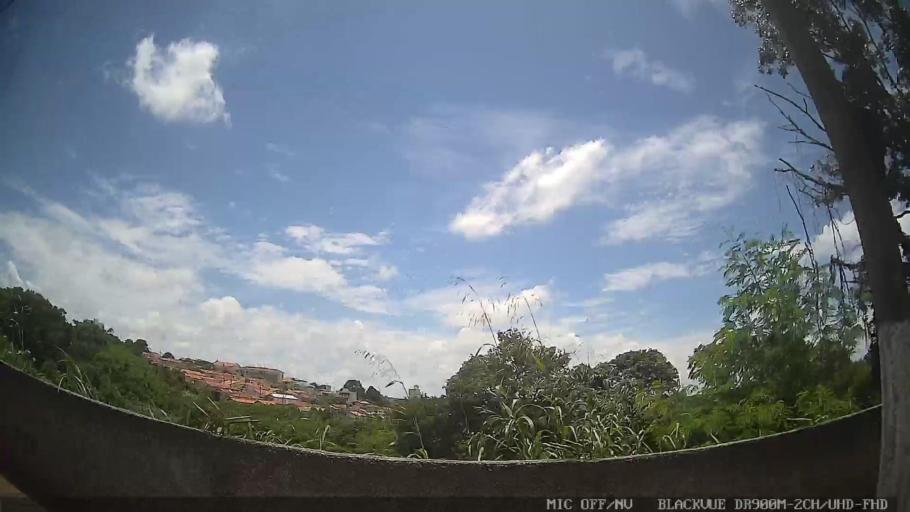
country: BR
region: Sao Paulo
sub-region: Laranjal Paulista
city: Laranjal Paulista
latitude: -23.0525
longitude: -47.8316
